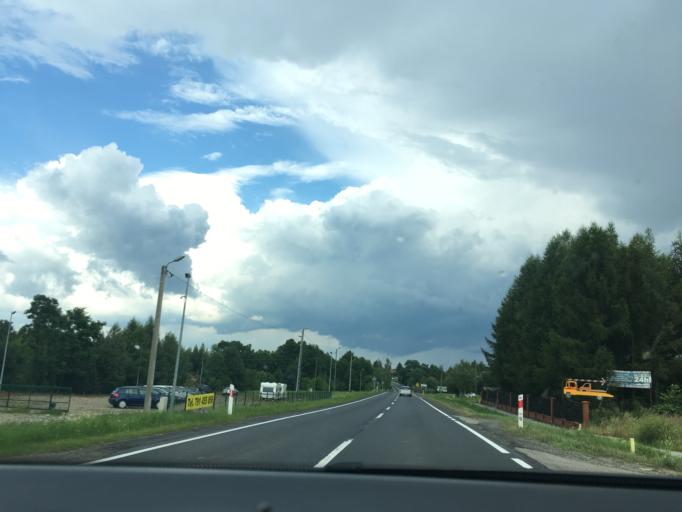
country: PL
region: Subcarpathian Voivodeship
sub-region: Powiat krosnienski
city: Kroscienko Wyzne
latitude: 49.6550
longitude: 21.8279
